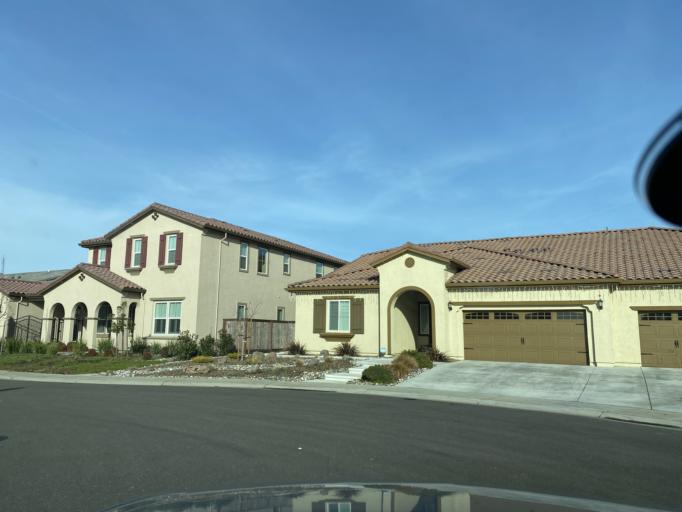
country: US
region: California
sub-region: Sacramento County
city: Elk Grove
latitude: 38.3959
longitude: -121.3901
